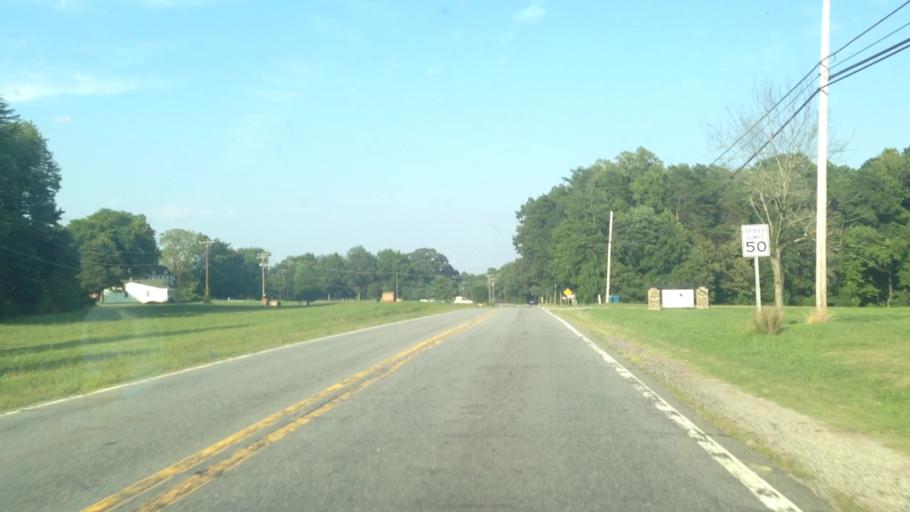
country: US
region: North Carolina
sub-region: Guilford County
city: Stokesdale
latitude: 36.2386
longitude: -79.9390
